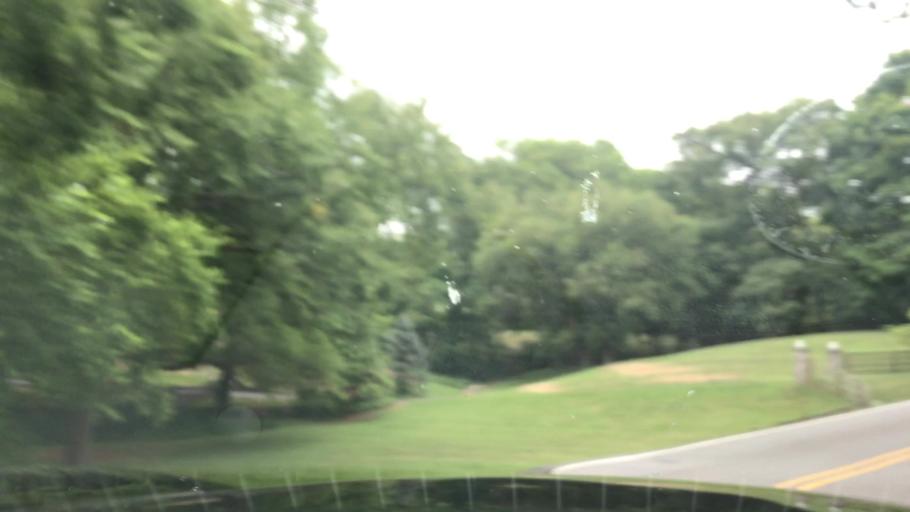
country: US
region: Tennessee
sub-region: Williamson County
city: Brentwood
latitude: 36.0351
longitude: -86.7688
